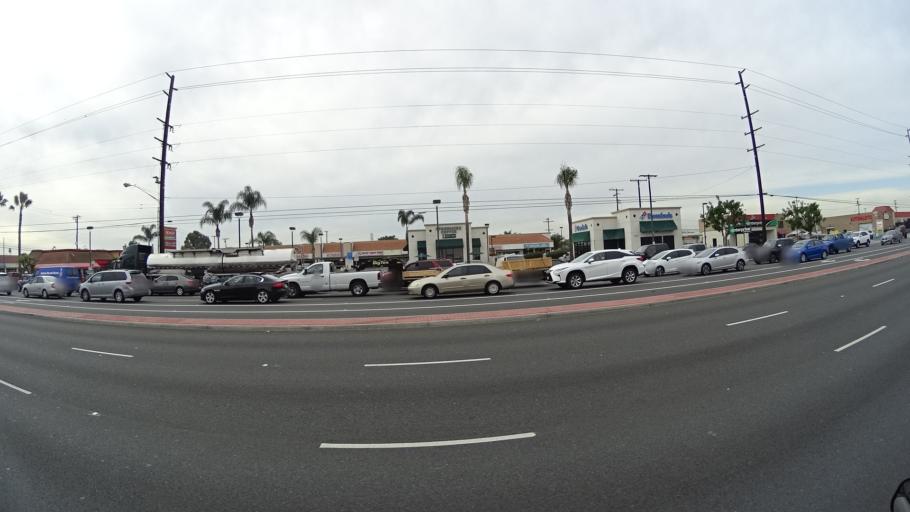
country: US
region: California
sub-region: Orange County
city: Stanton
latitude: 33.7892
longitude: -117.9928
